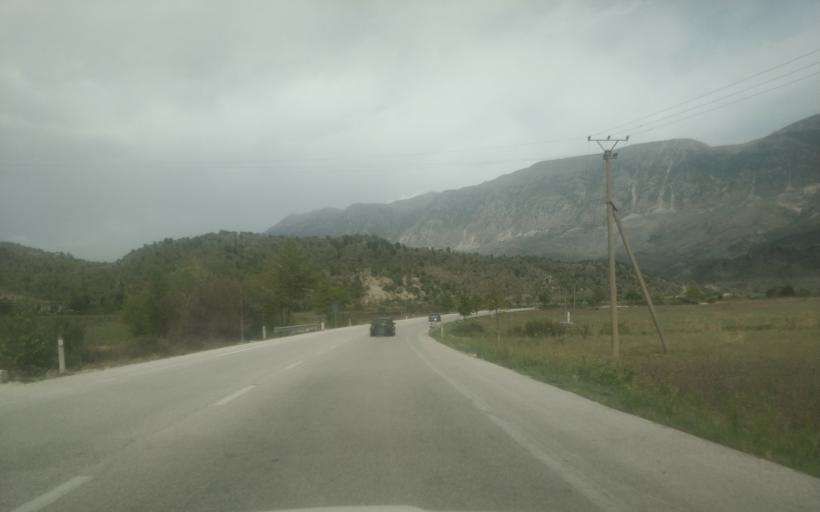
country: AL
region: Gjirokaster
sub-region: Rrethi i Gjirokastres
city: Picar
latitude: 40.1947
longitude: 20.0825
